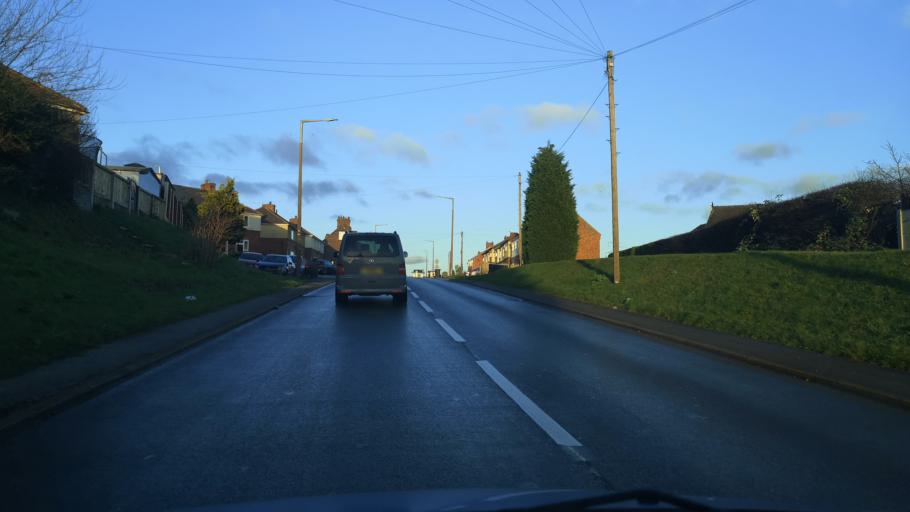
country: GB
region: England
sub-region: Barnsley
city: Little Houghton
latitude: 53.5397
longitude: -1.3512
